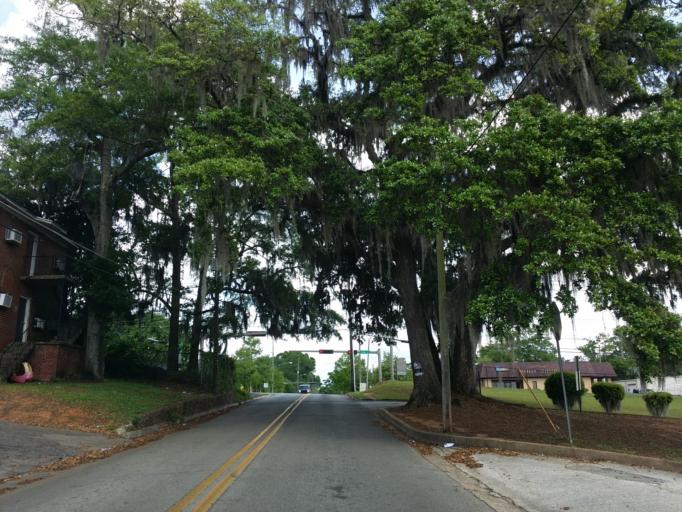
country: US
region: Florida
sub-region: Leon County
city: Tallahassee
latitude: 30.4199
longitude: -84.2829
